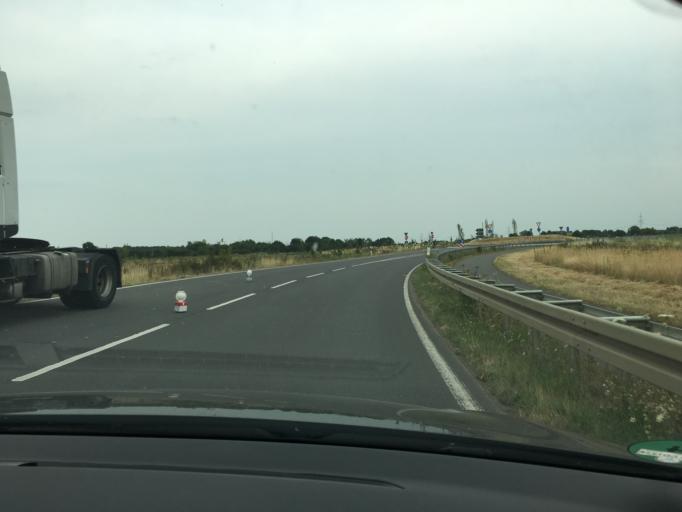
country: DE
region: North Rhine-Westphalia
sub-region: Regierungsbezirk Koln
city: Merzenich
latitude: 50.8493
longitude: 6.5140
